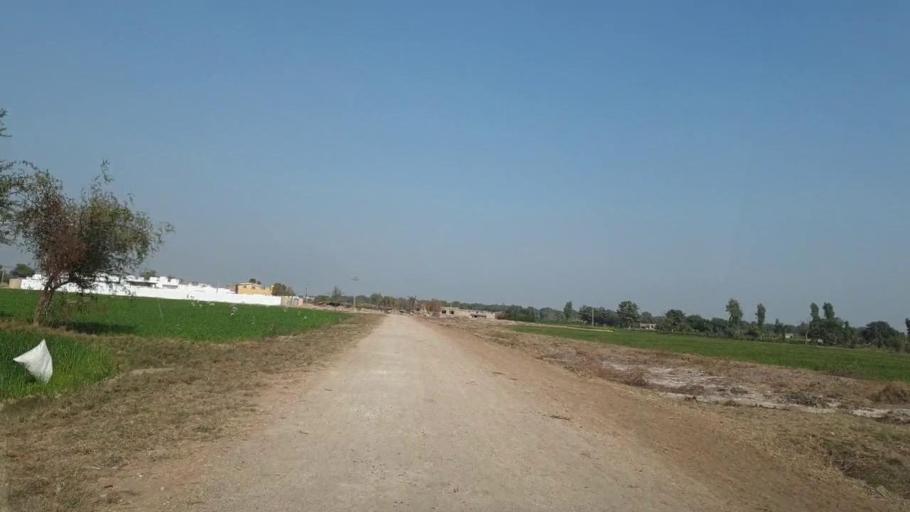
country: PK
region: Sindh
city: Matiari
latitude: 25.5052
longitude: 68.4584
